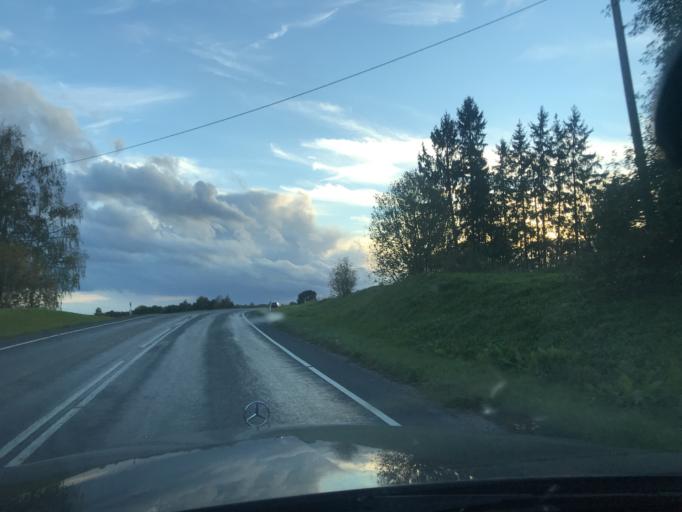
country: EE
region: Vorumaa
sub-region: Antsla vald
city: Vana-Antsla
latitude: 57.8737
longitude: 26.6261
